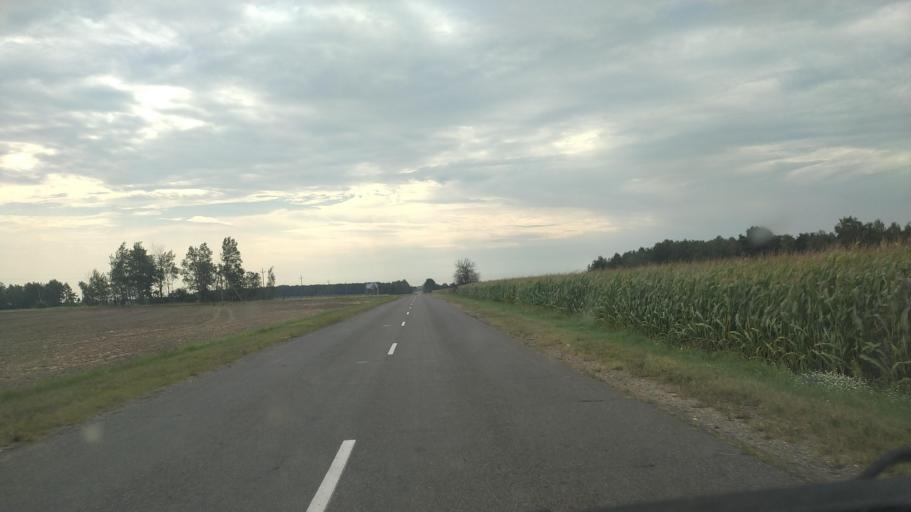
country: BY
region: Brest
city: Byaroza
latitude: 52.5670
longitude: 24.8980
